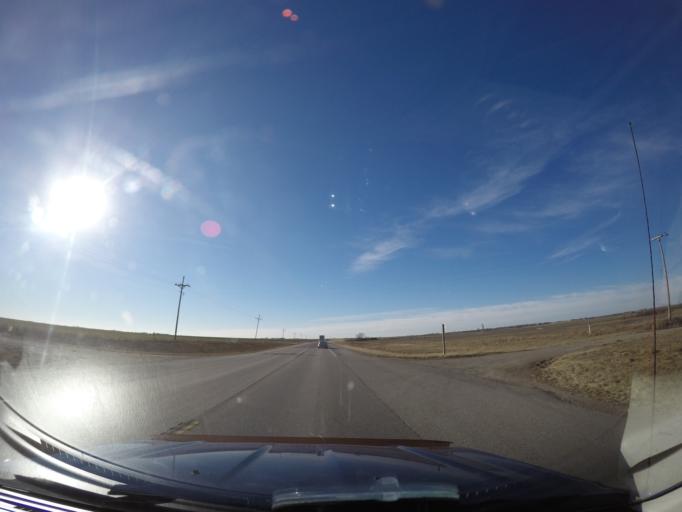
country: US
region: Kansas
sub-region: Marion County
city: Hillsboro
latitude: 38.3623
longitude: -97.2790
